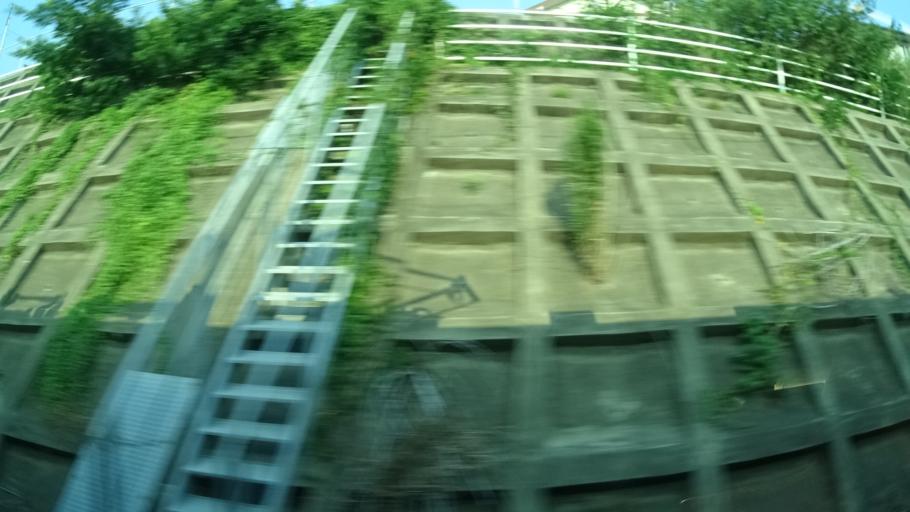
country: JP
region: Ibaraki
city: Hitachi
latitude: 36.6044
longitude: 140.6673
